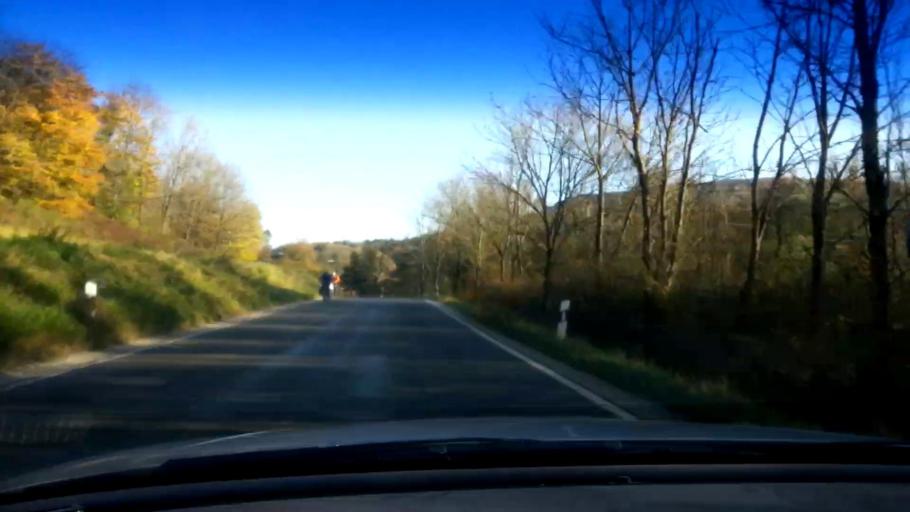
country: DE
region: Bavaria
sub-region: Upper Franconia
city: Heiligenstadt
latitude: 49.8778
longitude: 11.1357
